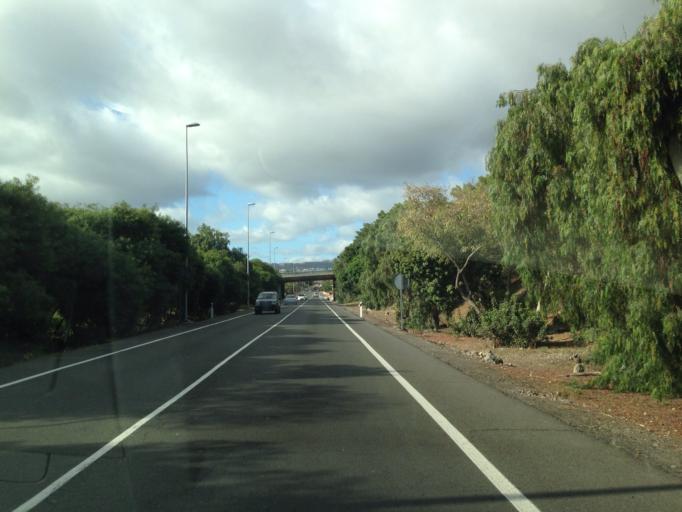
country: ES
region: Canary Islands
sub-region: Provincia de Las Palmas
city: Maspalomas
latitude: 27.7622
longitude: -15.5860
